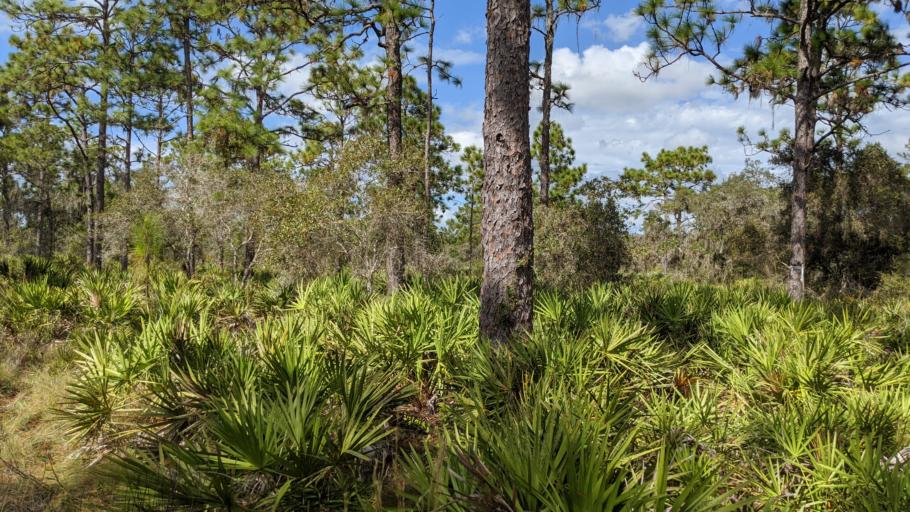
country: US
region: Florida
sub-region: Charlotte County
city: Cleveland
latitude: 26.9725
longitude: -81.9021
